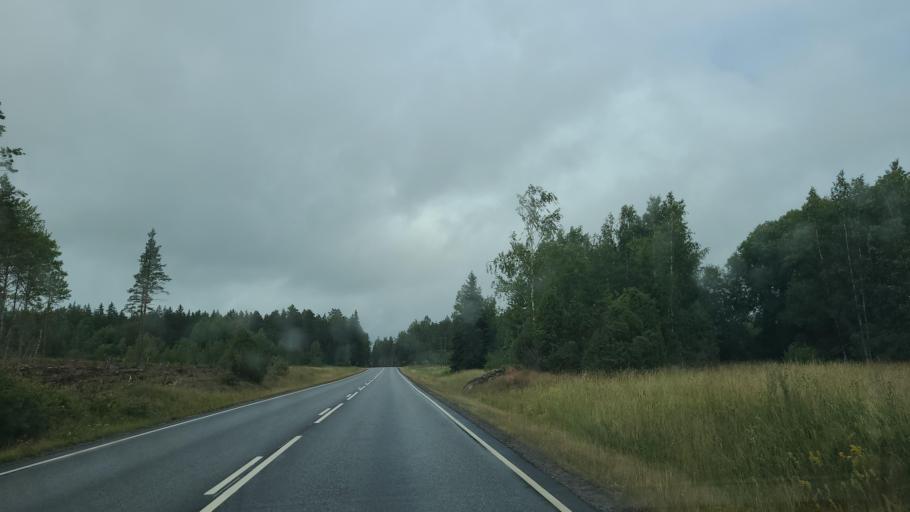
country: FI
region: Varsinais-Suomi
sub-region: Turku
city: Sauvo
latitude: 60.2415
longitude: 22.6123
